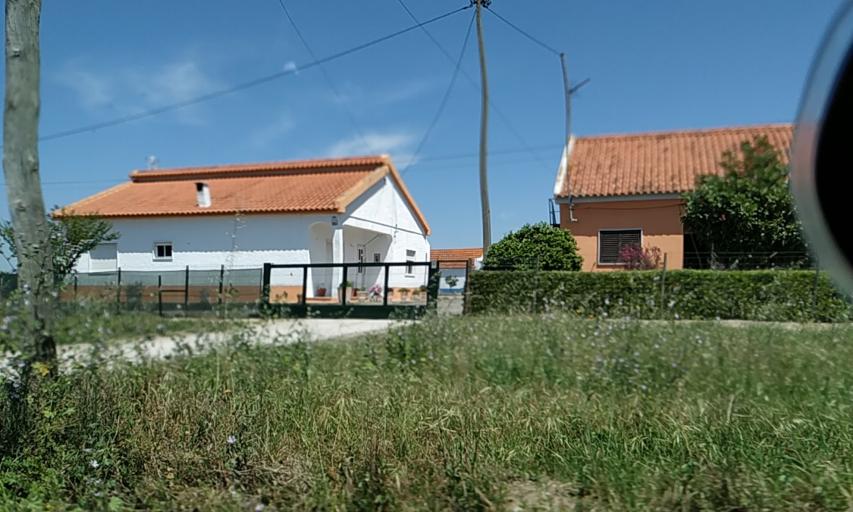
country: PT
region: Setubal
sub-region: Palmela
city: Pinhal Novo
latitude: 38.6399
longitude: -8.7424
